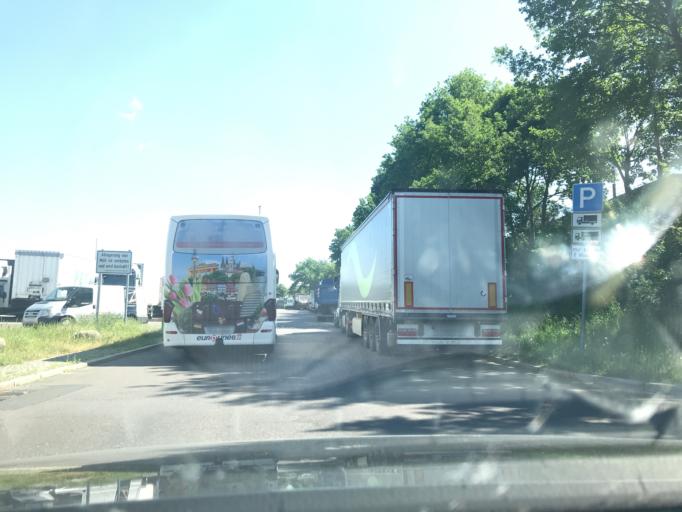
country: DE
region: Berlin
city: Westend
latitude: 52.4998
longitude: 13.2759
